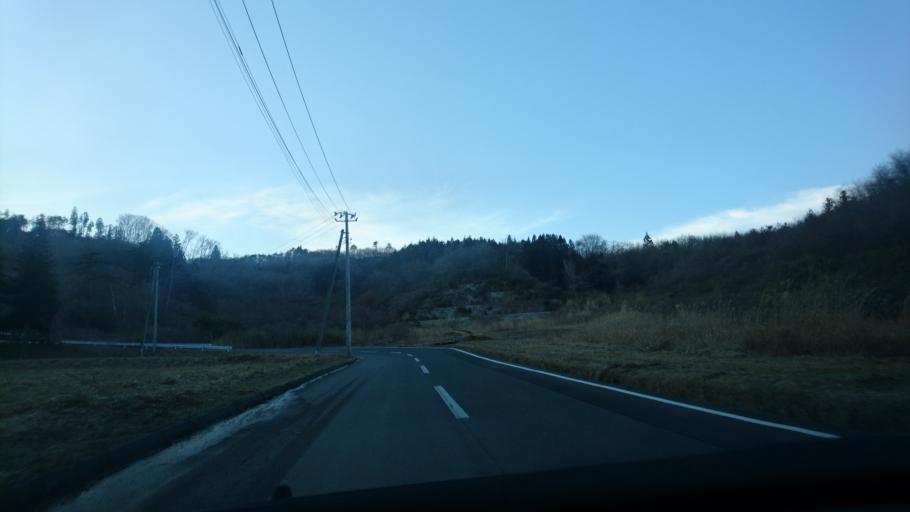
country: JP
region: Iwate
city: Mizusawa
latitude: 39.0398
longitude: 141.3263
